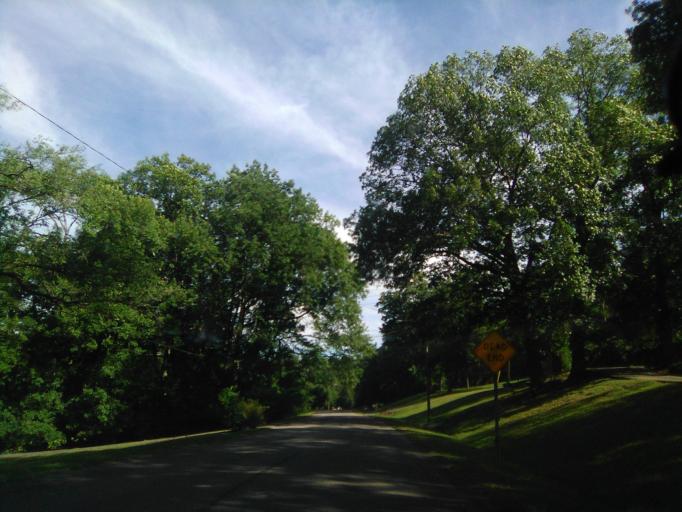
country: US
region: Tennessee
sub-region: Davidson County
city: Belle Meade
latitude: 36.1186
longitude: -86.9083
